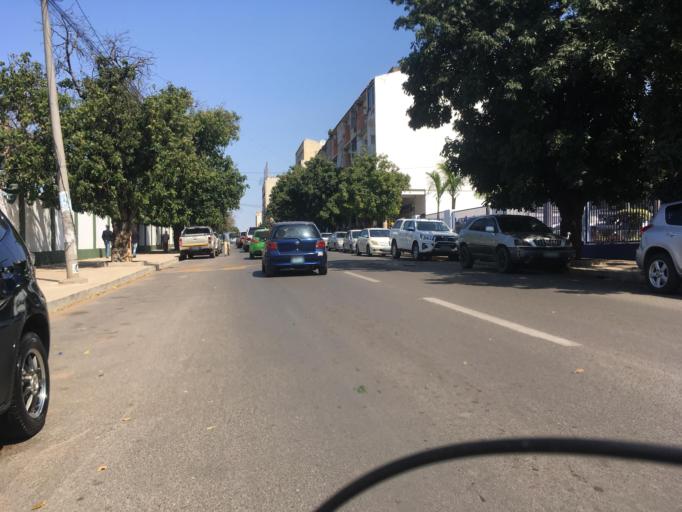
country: MZ
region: Maputo City
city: Maputo
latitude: -25.9605
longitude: 32.5751
